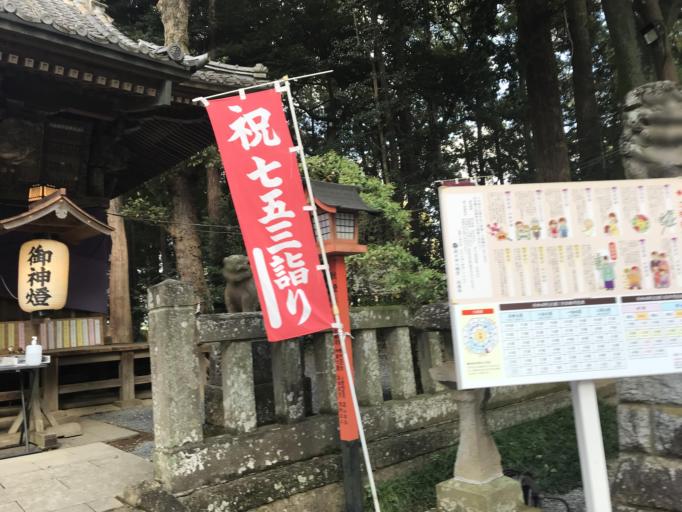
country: JP
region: Tochigi
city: Oyama
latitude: 36.2743
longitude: 139.7659
